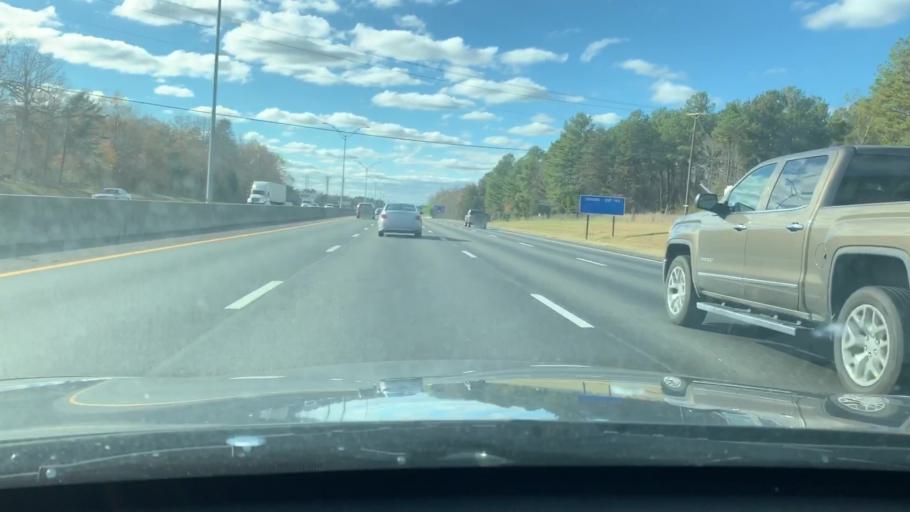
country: US
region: North Carolina
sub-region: Alamance County
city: Burlington
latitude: 36.0649
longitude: -79.4556
